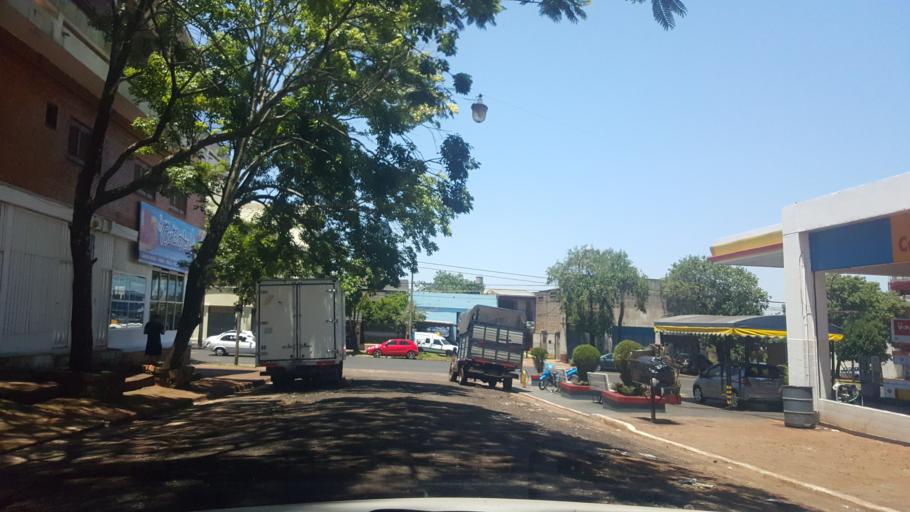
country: AR
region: Misiones
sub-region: Departamento de Capital
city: Posadas
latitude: -27.3911
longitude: -55.9090
